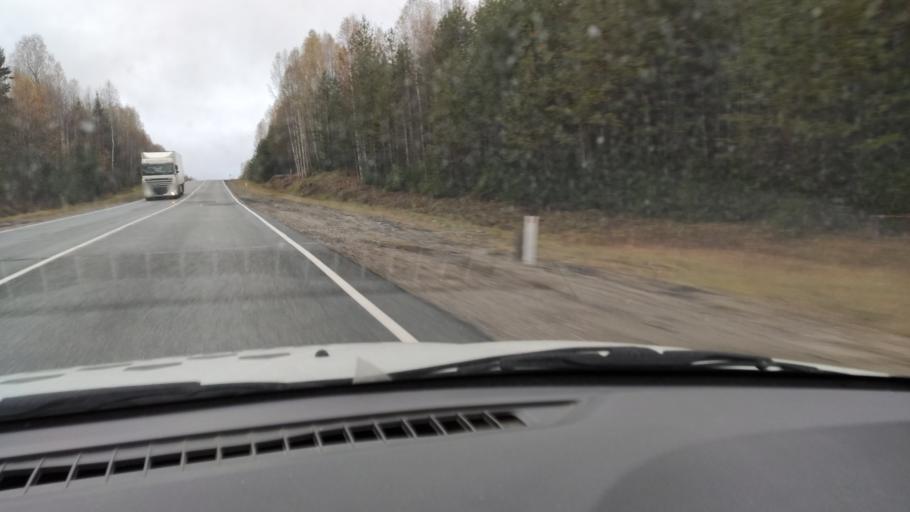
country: RU
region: Kirov
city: Chernaya Kholunitsa
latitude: 58.8930
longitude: 51.3373
